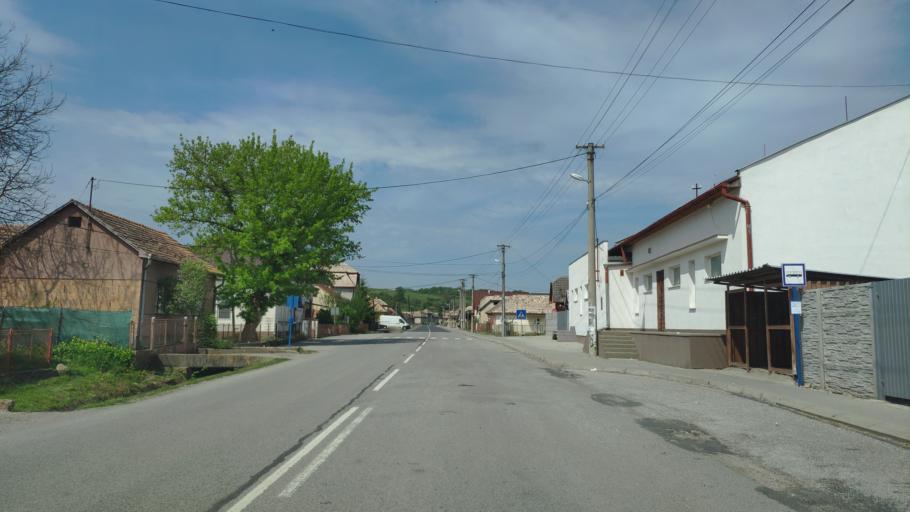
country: HU
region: Borsod-Abauj-Zemplen
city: Ozd
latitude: 48.3967
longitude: 20.2536
